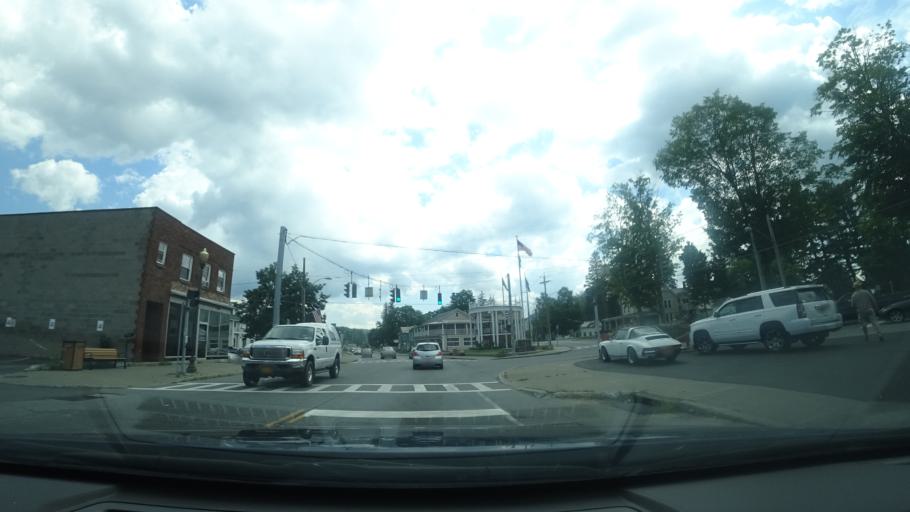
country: US
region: New York
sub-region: Warren County
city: Warrensburg
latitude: 43.4968
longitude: -73.7762
